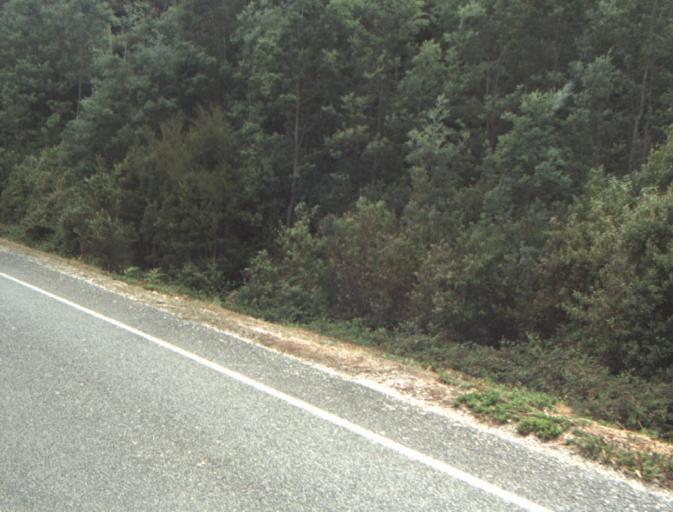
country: AU
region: Tasmania
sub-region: Launceston
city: Mayfield
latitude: -41.2802
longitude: 147.2200
